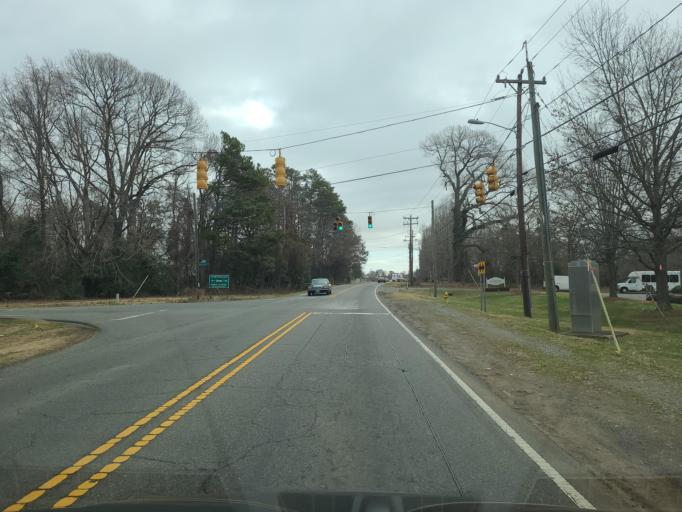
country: US
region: North Carolina
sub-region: Mecklenburg County
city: Mint Hill
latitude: 35.1895
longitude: -80.6972
